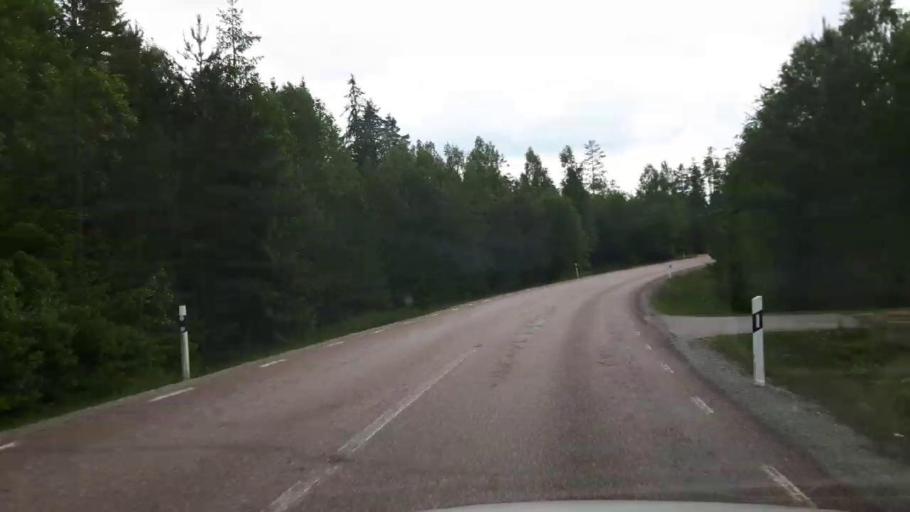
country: SE
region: Vaestmanland
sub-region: Skinnskattebergs Kommun
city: Skinnskatteberg
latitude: 59.8378
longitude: 15.8420
